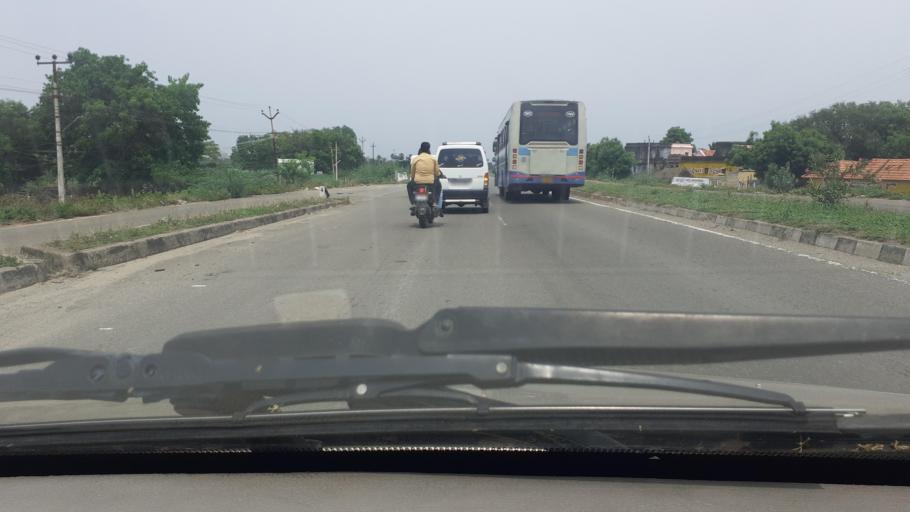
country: IN
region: Tamil Nadu
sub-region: Thoothukkudi
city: Srivaikuntam
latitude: 8.7365
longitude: 77.9207
